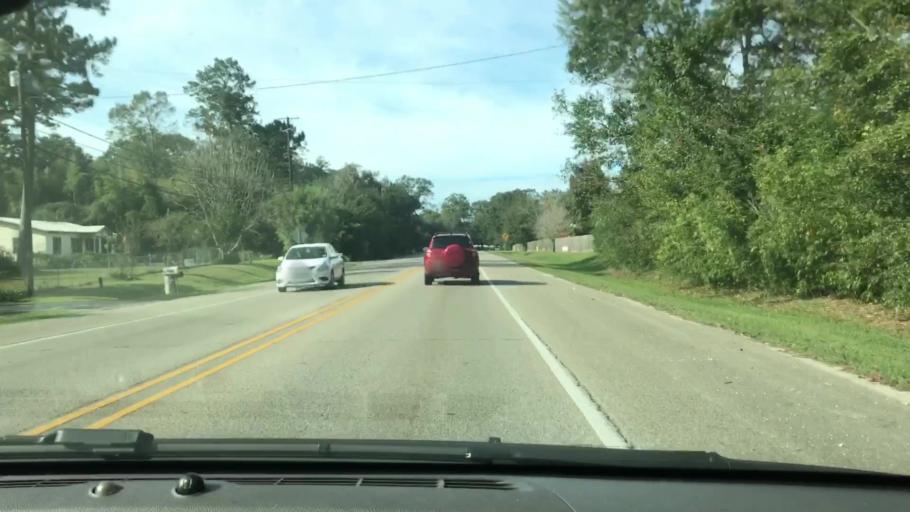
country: US
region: Louisiana
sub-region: Saint Tammany Parish
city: Pearl River
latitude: 30.3739
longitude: -89.7670
